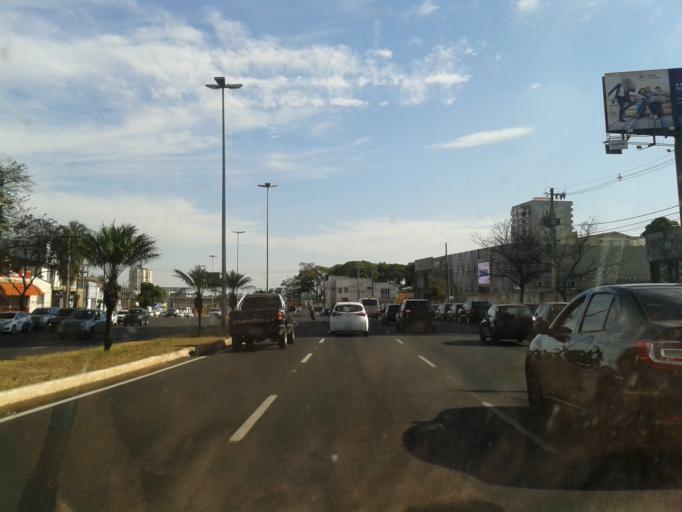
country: BR
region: Minas Gerais
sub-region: Uberlandia
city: Uberlandia
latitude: -18.9224
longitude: -48.2702
